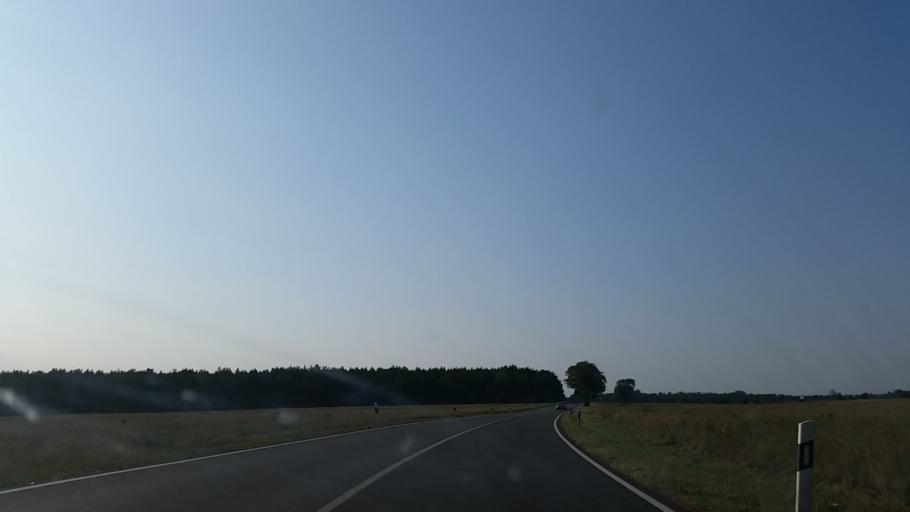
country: DE
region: Brandenburg
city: Passow
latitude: 53.1237
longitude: 14.1612
